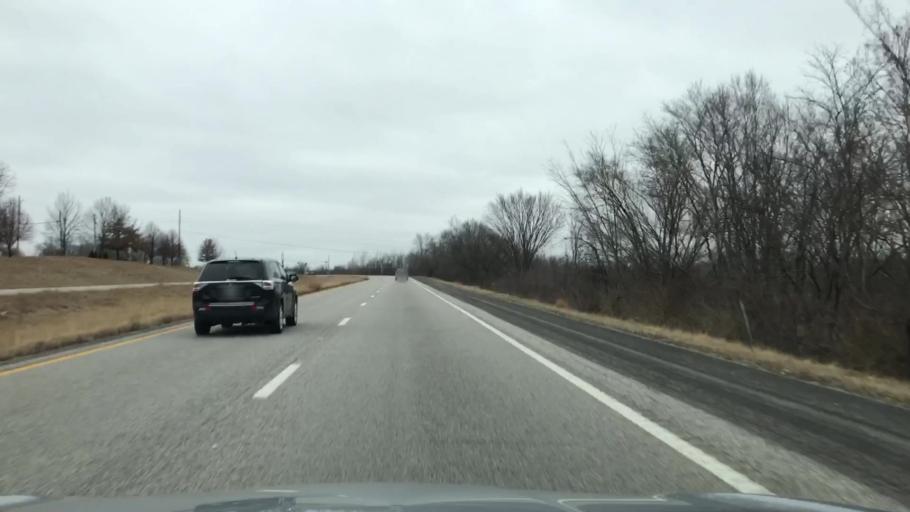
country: US
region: Missouri
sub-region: Clay County
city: Liberty
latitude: 39.2270
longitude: -94.4120
